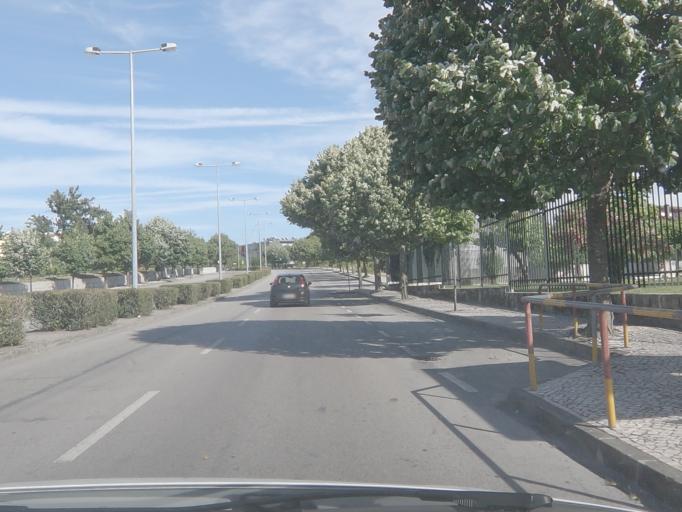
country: PT
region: Viseu
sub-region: Viseu
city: Viseu
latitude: 40.6425
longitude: -7.9203
